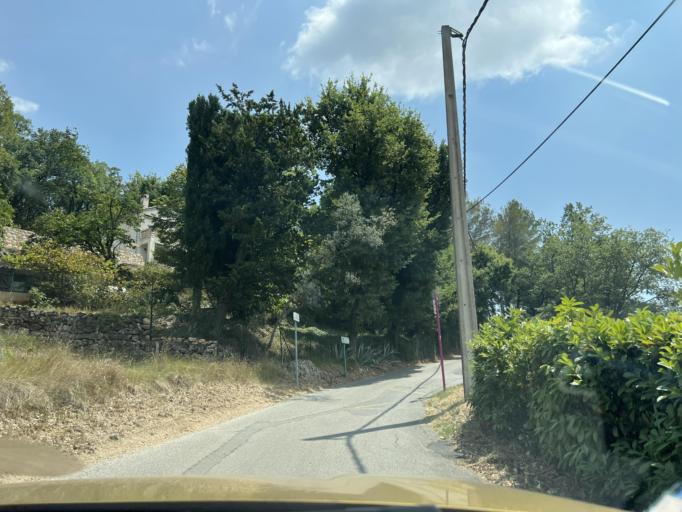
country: FR
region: Provence-Alpes-Cote d'Azur
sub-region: Departement des Alpes-Maritimes
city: Le Rouret
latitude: 43.7022
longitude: 7.0159
